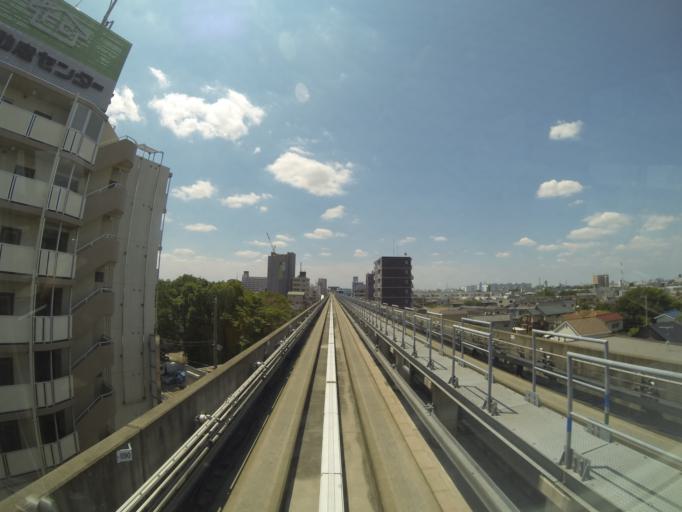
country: JP
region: Saitama
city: Soka
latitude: 35.8090
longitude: 139.7699
